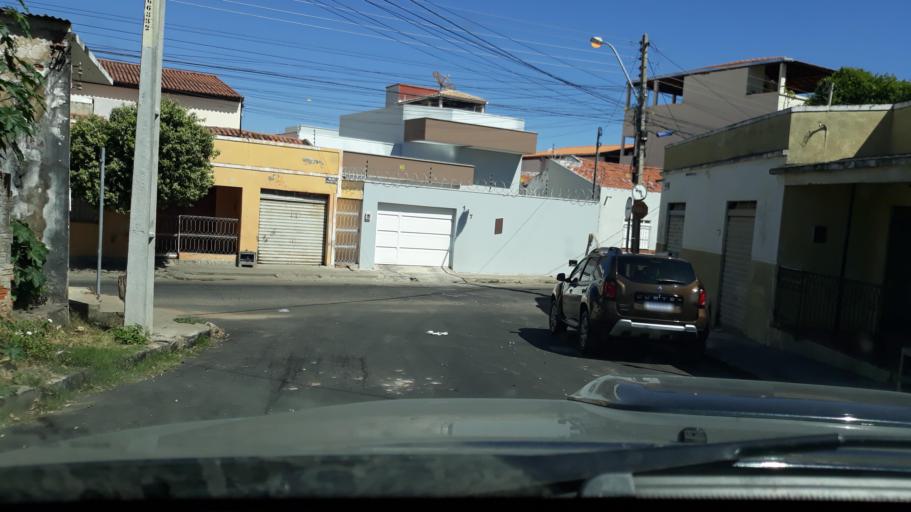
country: BR
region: Bahia
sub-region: Guanambi
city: Guanambi
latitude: -14.2271
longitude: -42.7827
